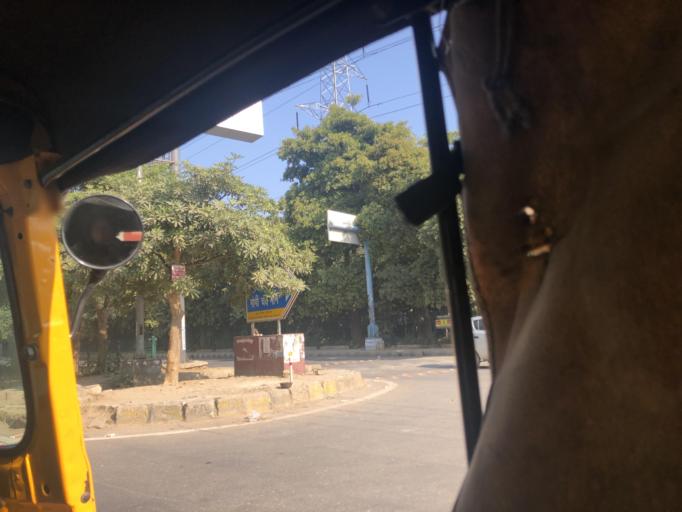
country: IN
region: Haryana
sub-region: Gurgaon
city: Gurgaon
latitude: 28.4323
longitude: 77.0910
